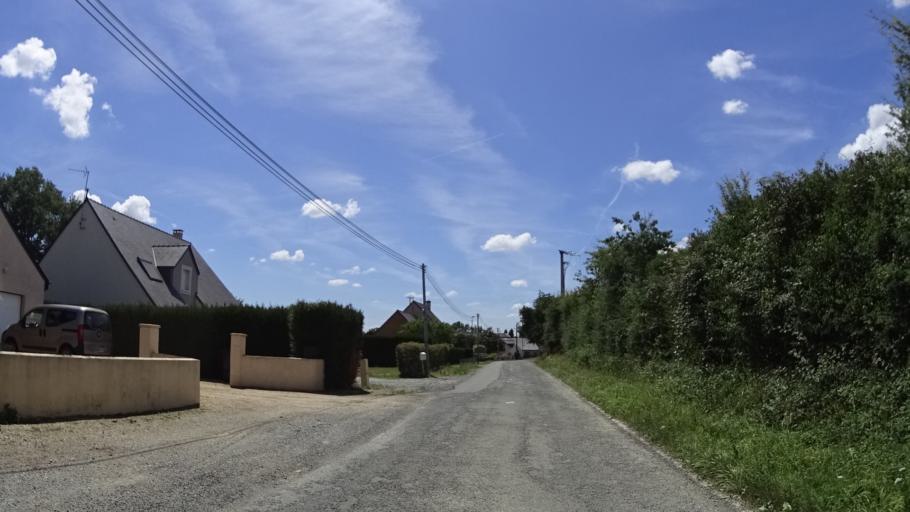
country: FR
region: Pays de la Loire
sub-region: Departement de Maine-et-Loire
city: Segre
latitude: 47.6207
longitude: -0.8861
